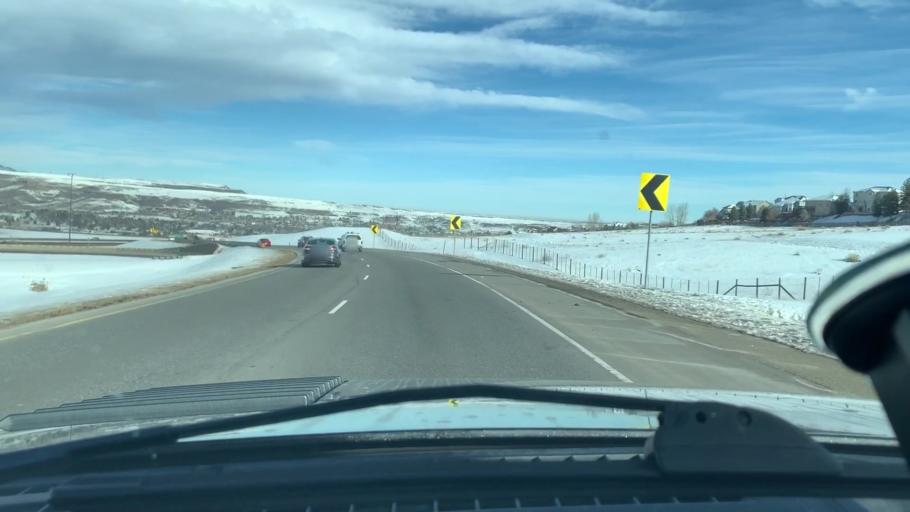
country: US
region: Colorado
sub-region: Jefferson County
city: West Pleasant View
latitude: 39.7110
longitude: -105.1913
